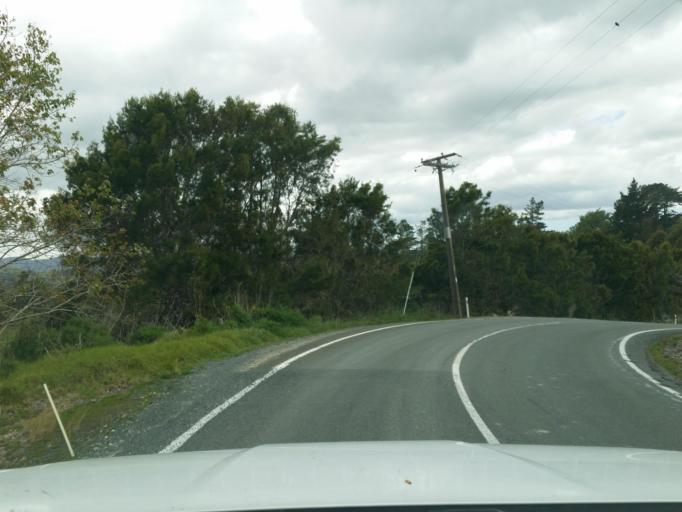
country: NZ
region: Auckland
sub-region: Auckland
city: Wellsford
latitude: -36.2255
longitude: 174.3732
